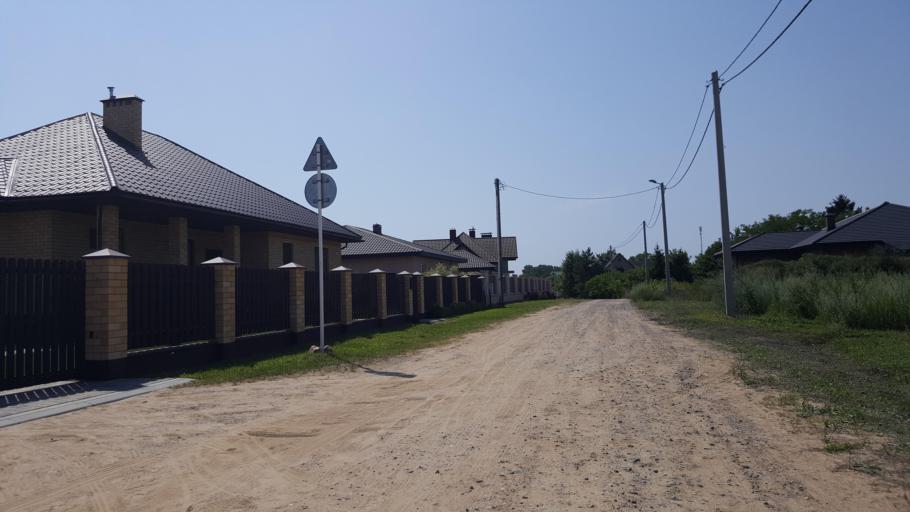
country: BY
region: Brest
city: Zhabinka
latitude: 52.1985
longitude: 23.9906
